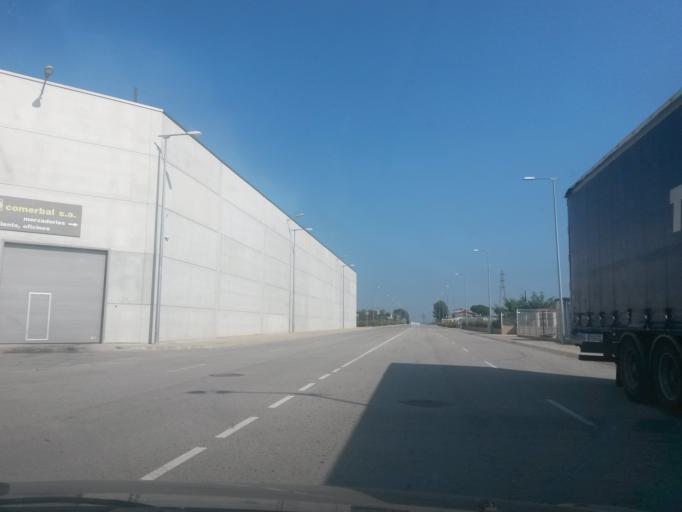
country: ES
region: Catalonia
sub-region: Provincia de Girona
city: Fornells de la Selva
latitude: 41.9370
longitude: 2.7961
